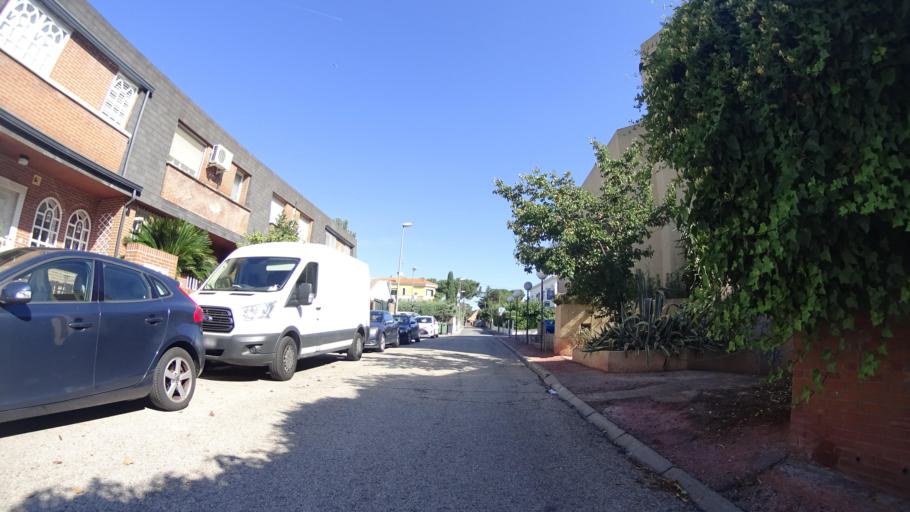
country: ES
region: Madrid
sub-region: Provincia de Madrid
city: Las Matas
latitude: 40.5475
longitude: -3.8908
